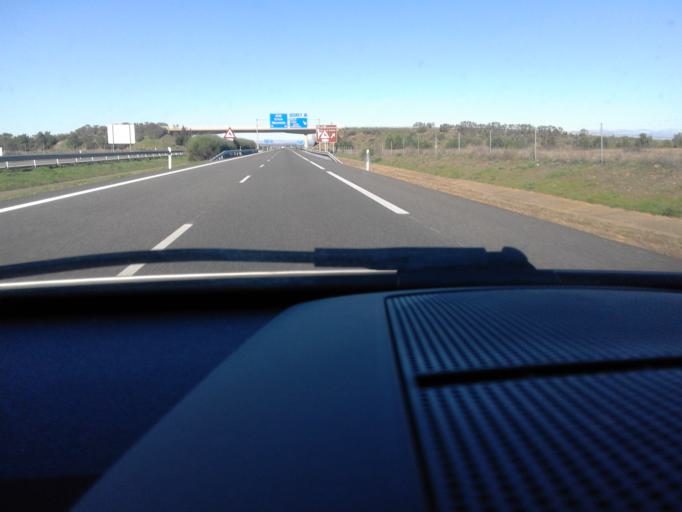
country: ES
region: Castille and Leon
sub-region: Provincia de Leon
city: Vega de Infanzones
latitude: 42.4912
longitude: -5.5584
